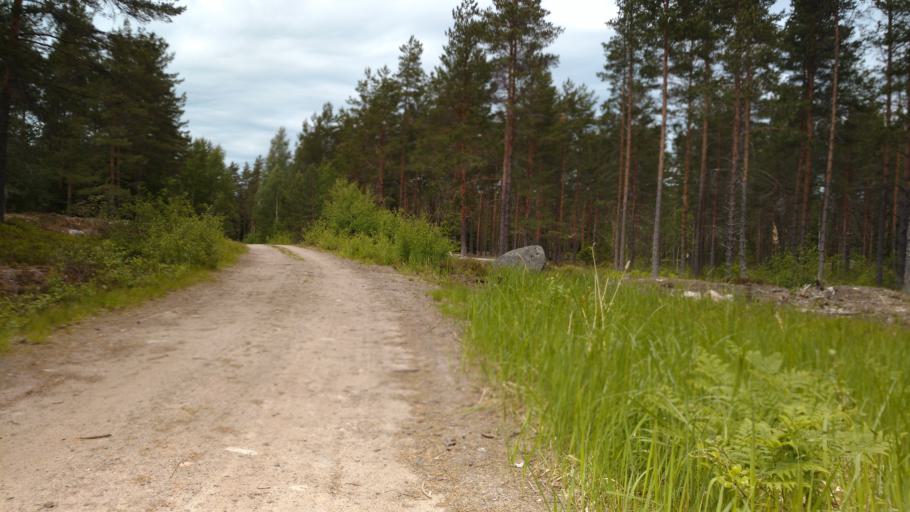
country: FI
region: Uusimaa
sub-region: Raaseporin
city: Pohja
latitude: 60.1142
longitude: 23.5540
